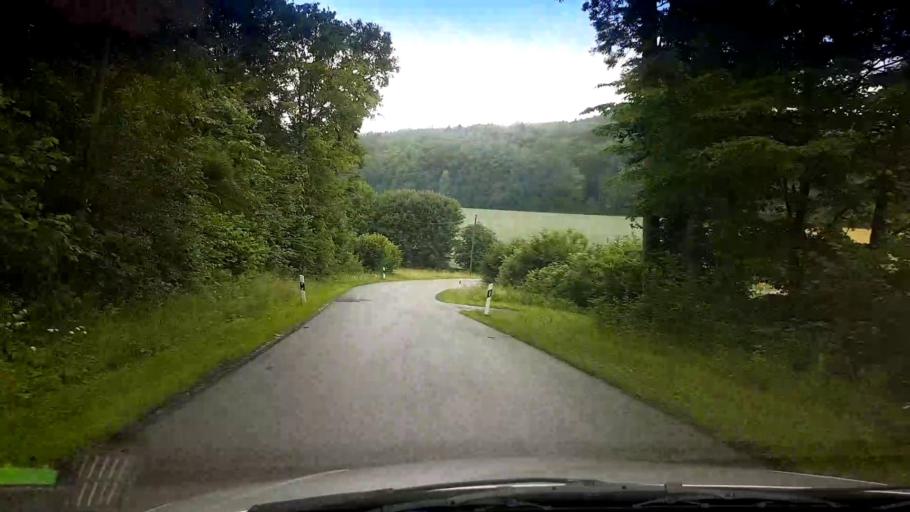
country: DE
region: Bavaria
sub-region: Upper Franconia
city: Altendorf
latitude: 50.0695
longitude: 11.1558
